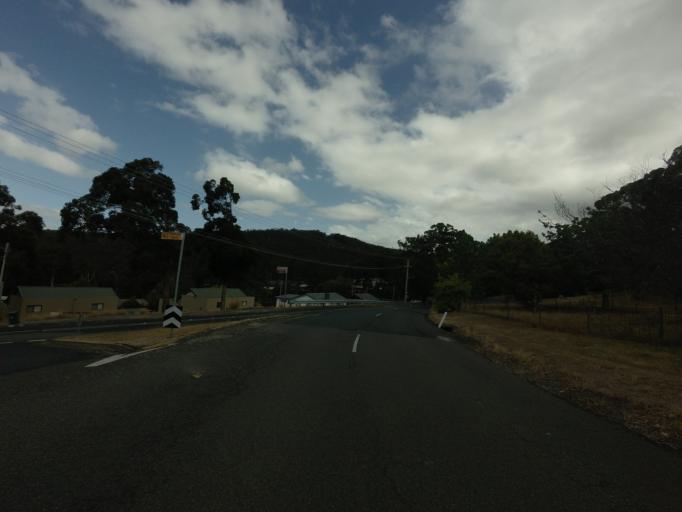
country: AU
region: Tasmania
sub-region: Hobart
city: Dynnyrne
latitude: -42.8997
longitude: 147.2756
